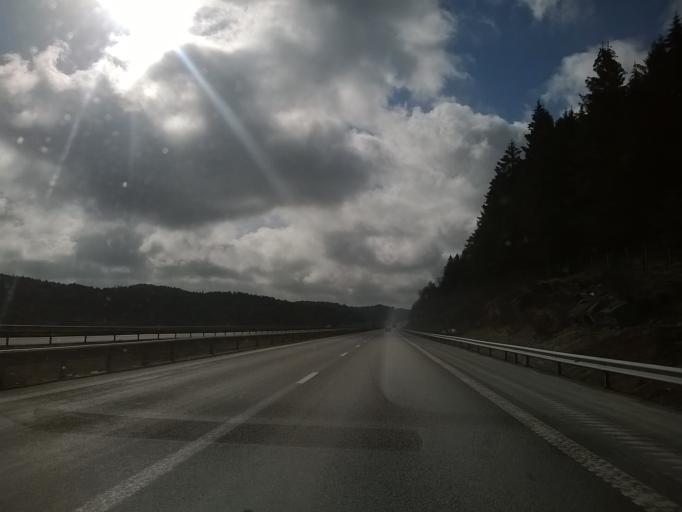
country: SE
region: Halland
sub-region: Kungsbacka Kommun
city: Frillesas
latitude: 57.3723
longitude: 12.2010
